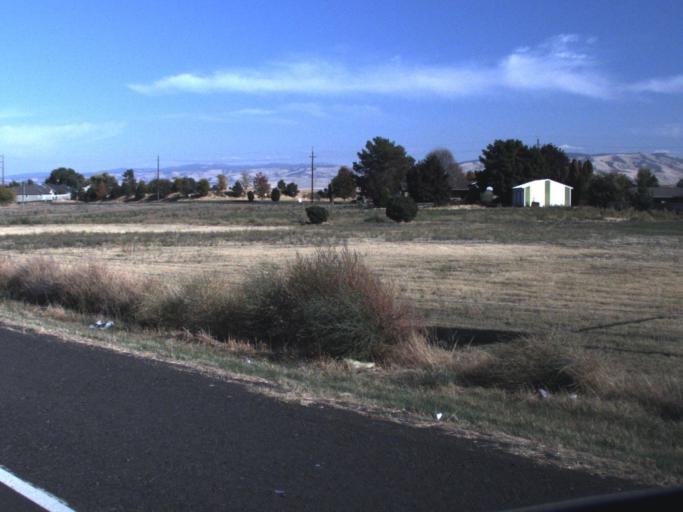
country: US
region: Washington
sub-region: Walla Walla County
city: College Place
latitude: 46.0300
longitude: -118.3837
